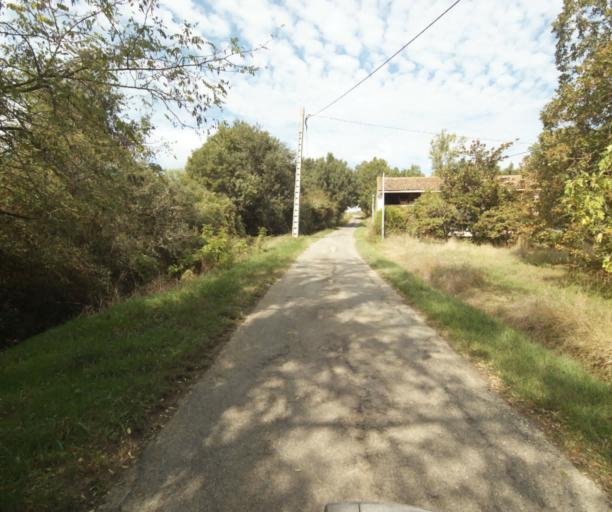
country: FR
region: Midi-Pyrenees
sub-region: Departement du Tarn-et-Garonne
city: Verdun-sur-Garonne
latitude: 43.8561
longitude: 1.1793
